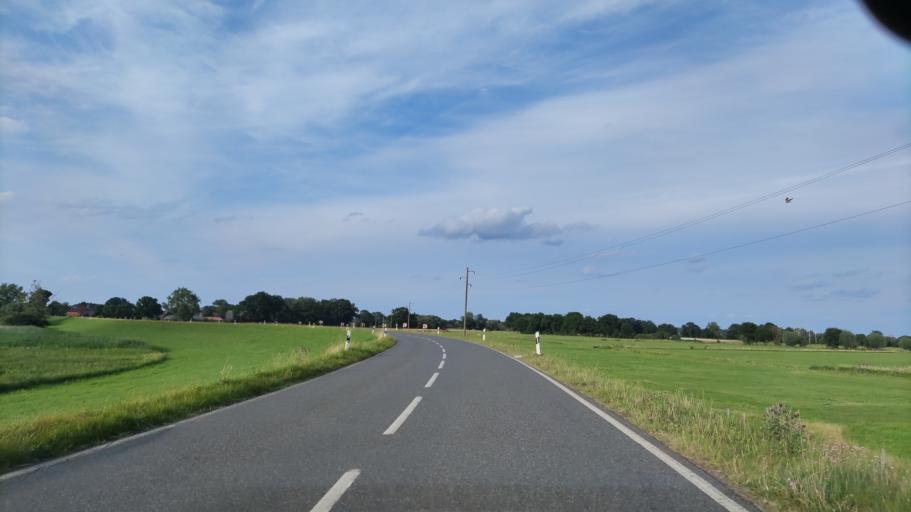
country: DE
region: Lower Saxony
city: Dannenberg
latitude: 53.1306
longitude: 11.1198
